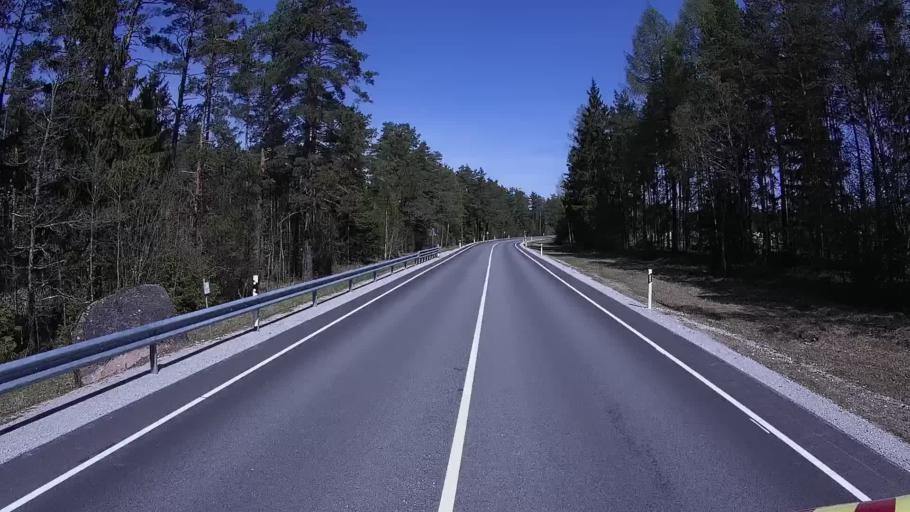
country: EE
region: Laeaene
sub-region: Ridala Parish
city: Uuemoisa
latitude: 59.0396
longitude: 23.8297
